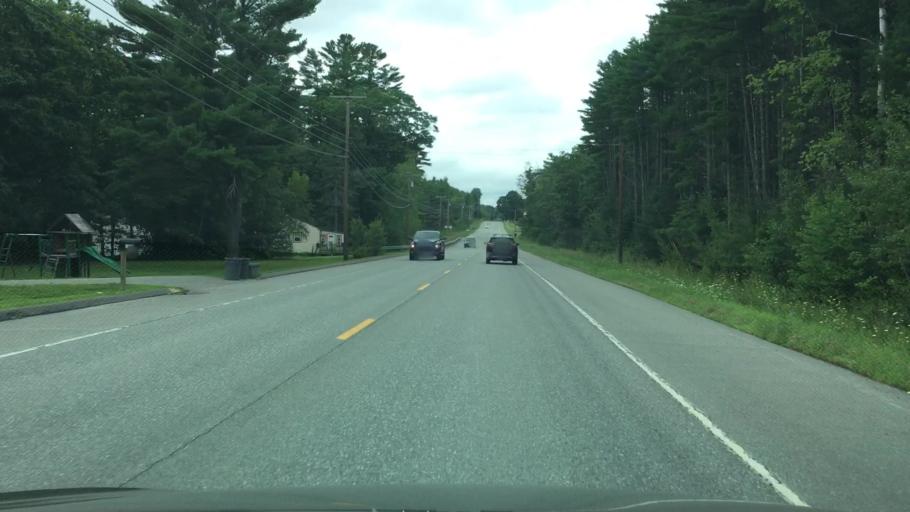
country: US
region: Maine
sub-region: Penobscot County
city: Orrington
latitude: 44.7067
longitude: -68.8238
